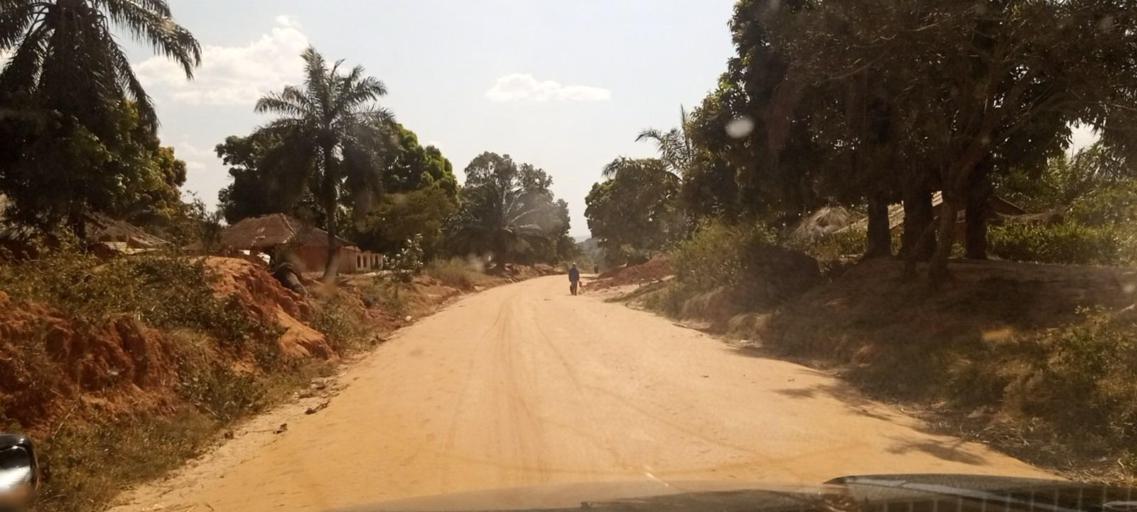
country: CD
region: Kasai-Oriental
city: Kabinda
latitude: -6.1309
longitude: 24.5238
